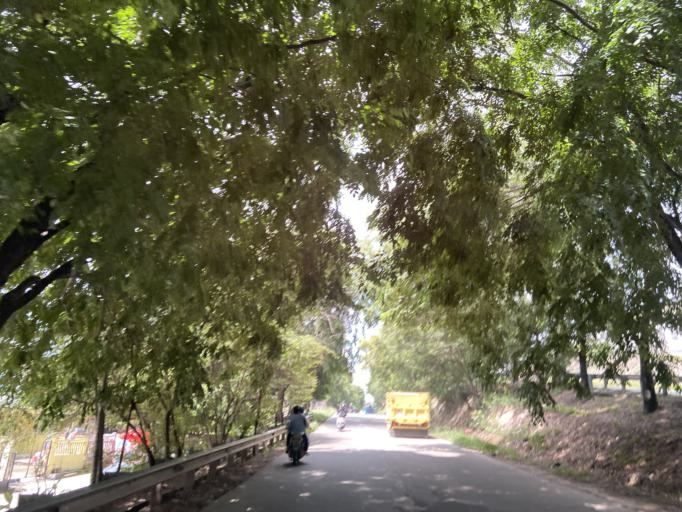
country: SG
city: Singapore
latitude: 1.1348
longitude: 104.0031
